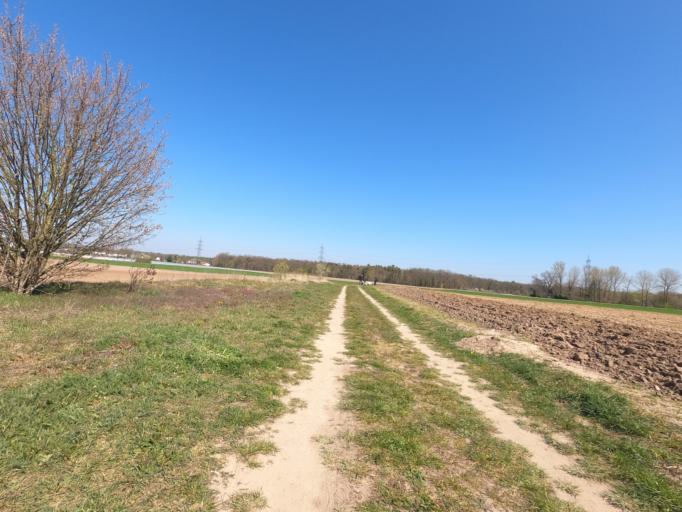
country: DE
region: Hesse
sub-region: Regierungsbezirk Darmstadt
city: Gross-Gerau
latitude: 49.9316
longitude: 8.5024
